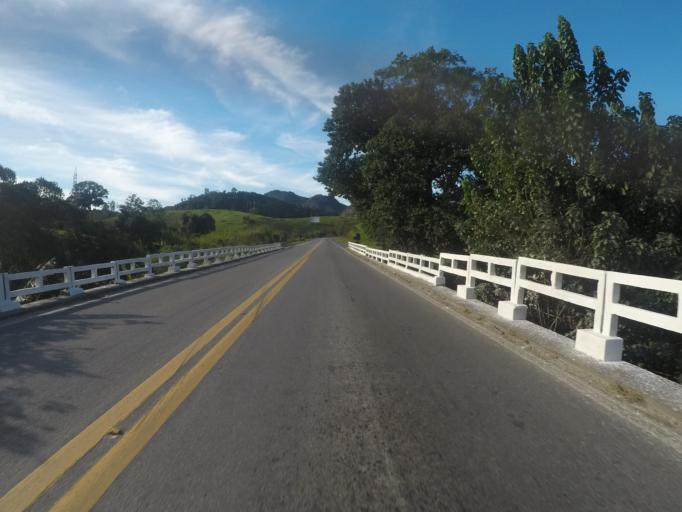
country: BR
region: Espirito Santo
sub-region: Ibiracu
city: Ibiracu
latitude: -19.8732
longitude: -40.4129
